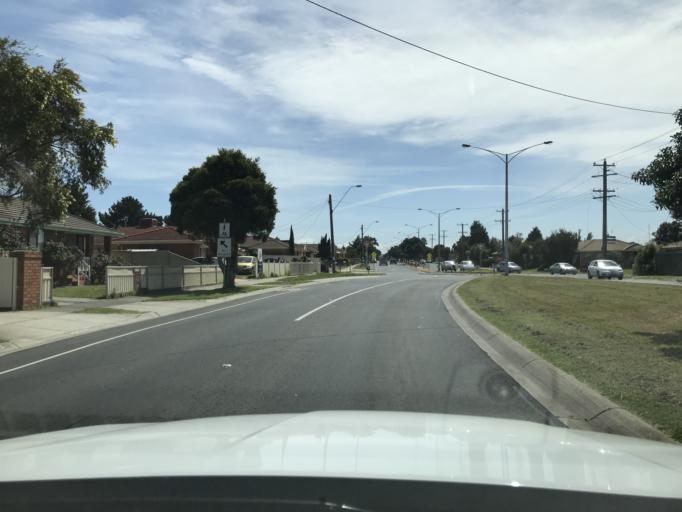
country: AU
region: Victoria
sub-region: Hume
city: Roxburgh Park
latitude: -37.6101
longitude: 144.9278
